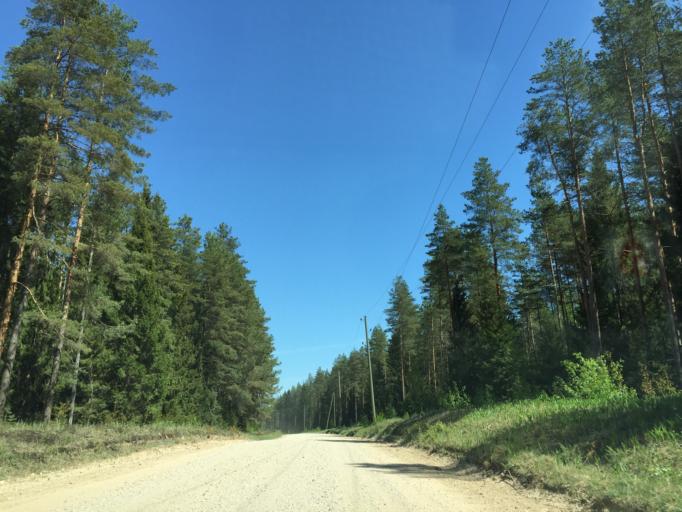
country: LV
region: Ogre
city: Ogre
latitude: 56.7459
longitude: 24.5781
